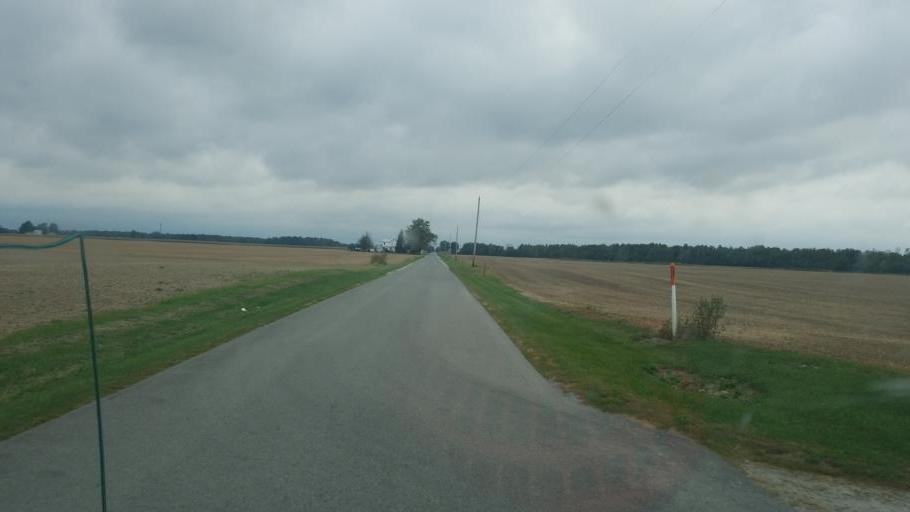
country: US
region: Ohio
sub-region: Seneca County
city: Fostoria
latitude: 41.0827
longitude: -83.5167
